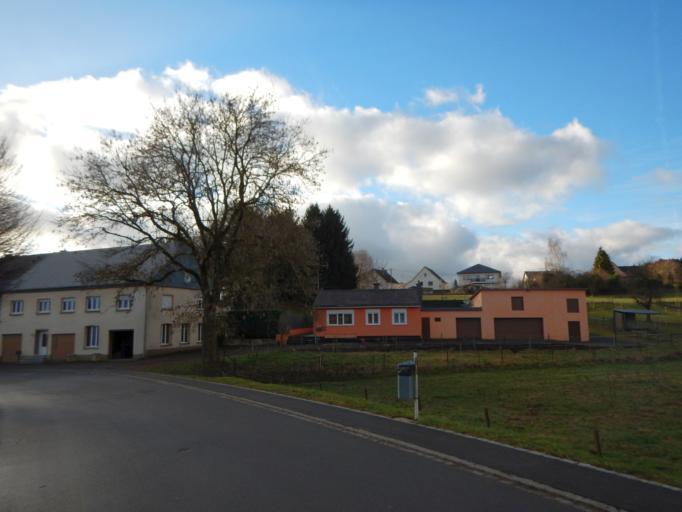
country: LU
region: Diekirch
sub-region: Canton de Redange
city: Redange-sur-Attert
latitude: 49.7678
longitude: 5.8923
